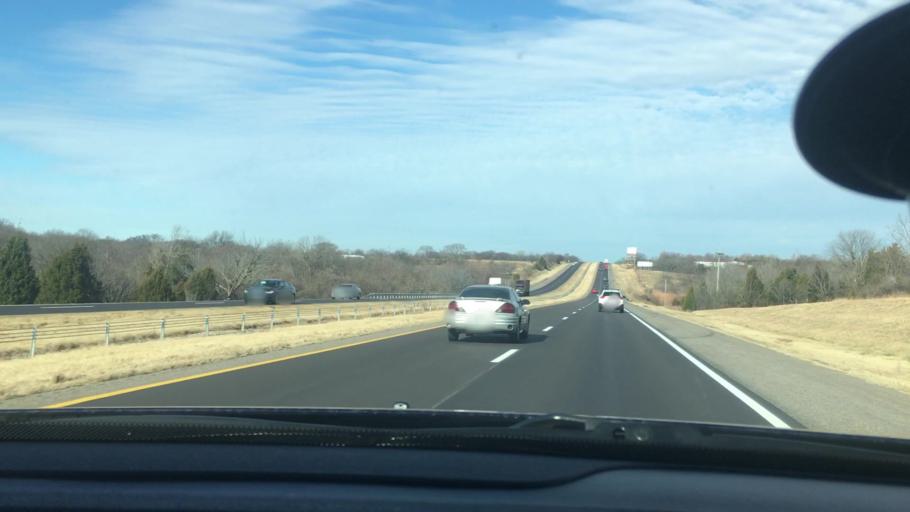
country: US
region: Oklahoma
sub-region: Cleveland County
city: Noble
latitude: 35.1008
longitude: -97.4282
